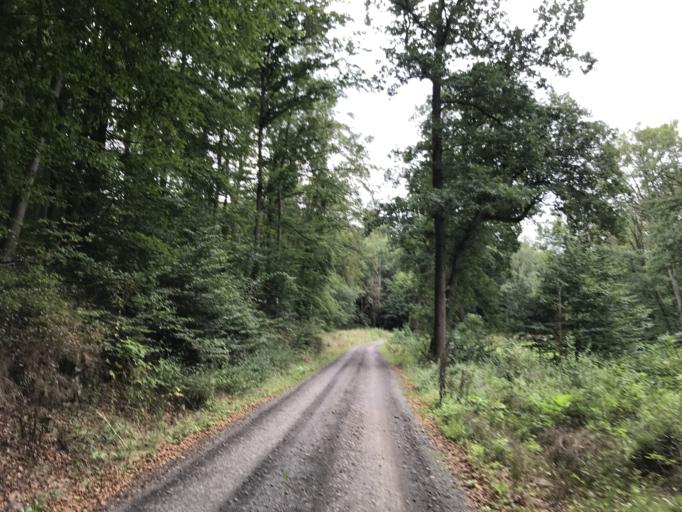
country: DE
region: Hesse
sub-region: Regierungsbezirk Giessen
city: Laubach
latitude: 50.5731
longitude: 8.9922
